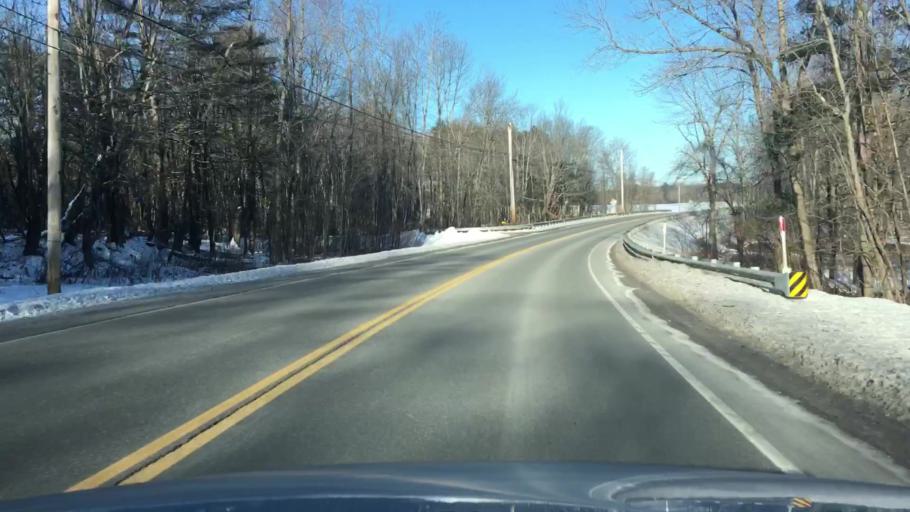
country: US
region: Maine
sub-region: Androscoggin County
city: Lisbon
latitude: 43.9858
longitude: -70.1355
